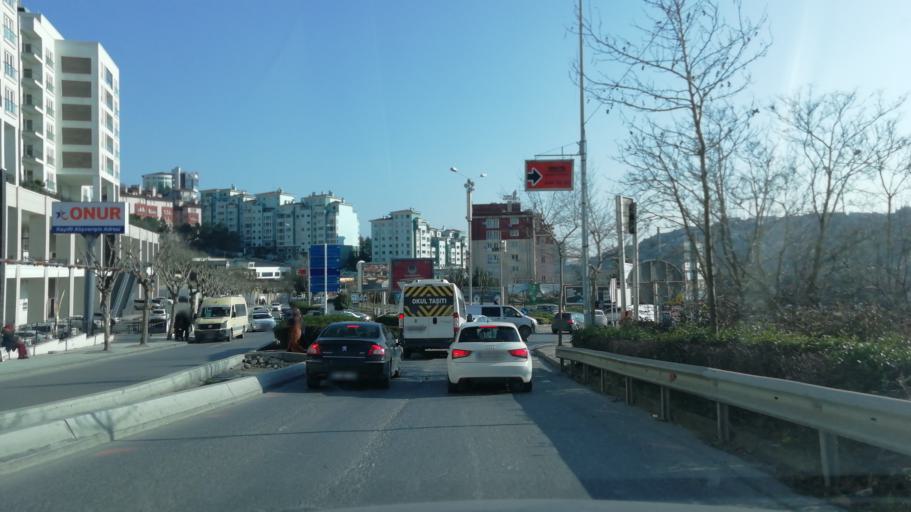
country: TR
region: Istanbul
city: Esenyurt
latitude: 41.0736
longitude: 28.6924
